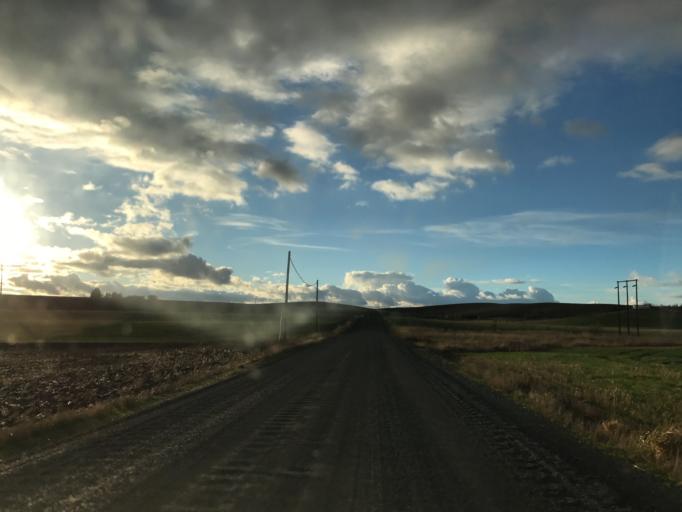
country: US
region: Idaho
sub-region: Latah County
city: Moscow
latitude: 46.7733
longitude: -116.9732
